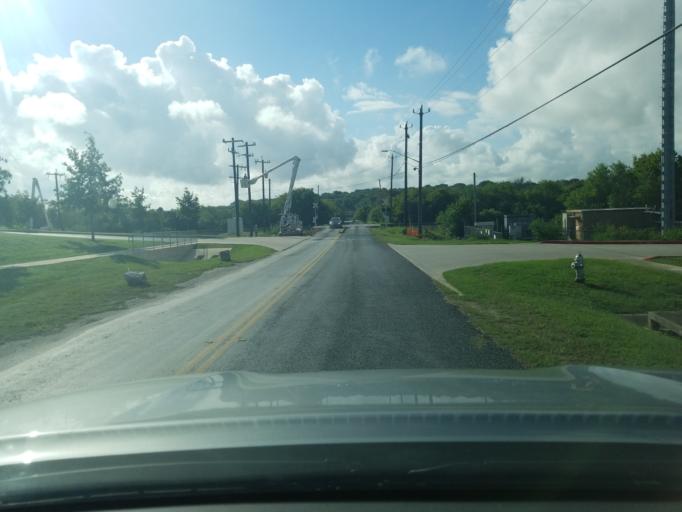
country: US
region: Texas
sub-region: Bexar County
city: Live Oak
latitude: 29.5982
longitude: -98.3630
